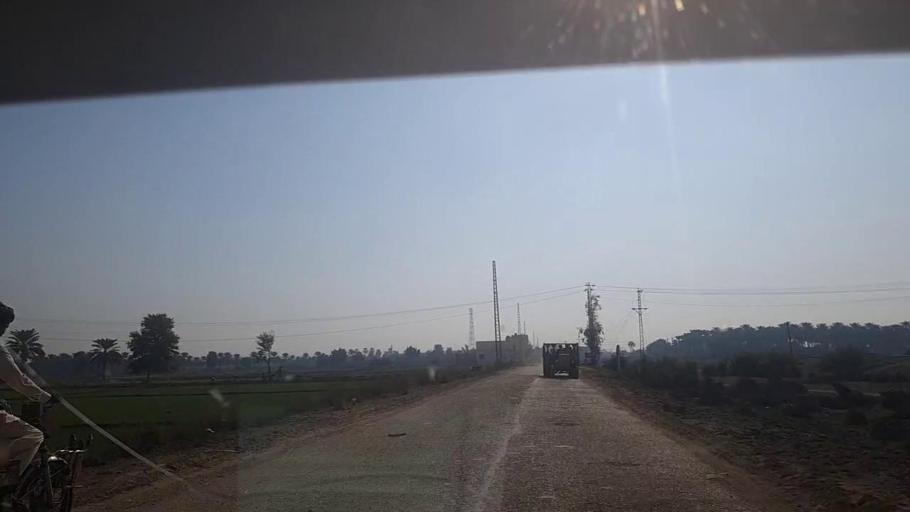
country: PK
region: Sindh
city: Gambat
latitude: 27.3483
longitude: 68.5493
